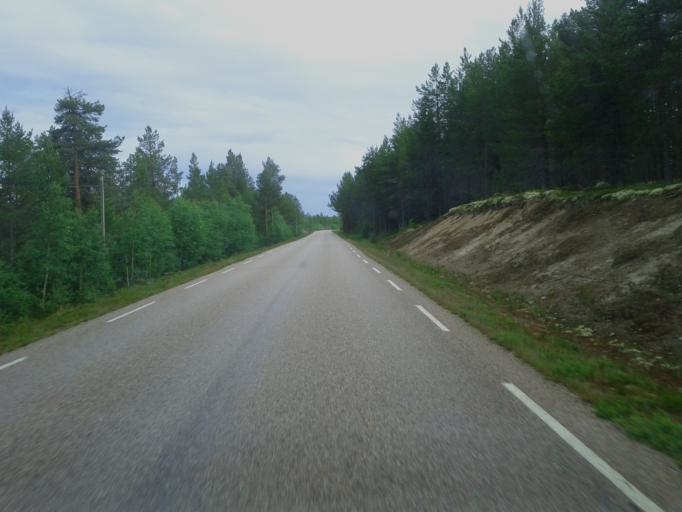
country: NO
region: Hedmark
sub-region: Engerdal
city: Engerdal
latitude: 62.0693
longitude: 11.6773
